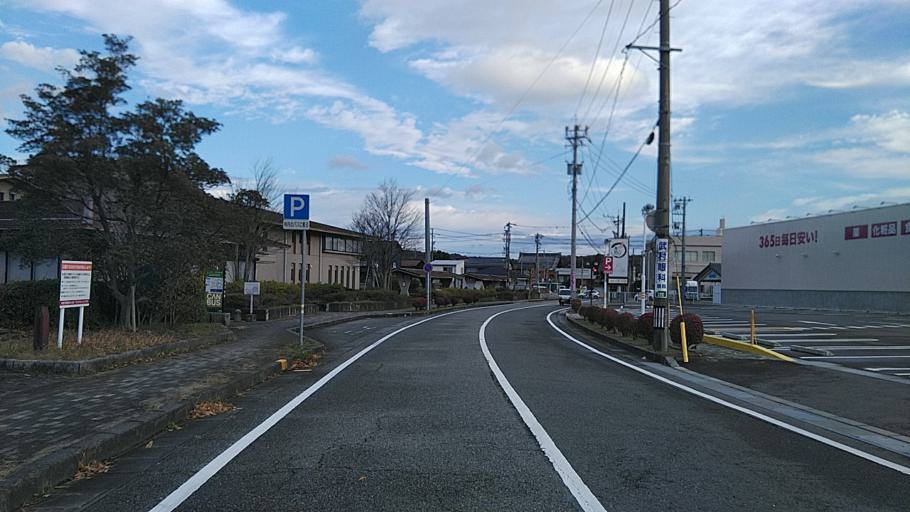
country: JP
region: Fukui
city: Maruoka
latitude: 36.3019
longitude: 136.3111
